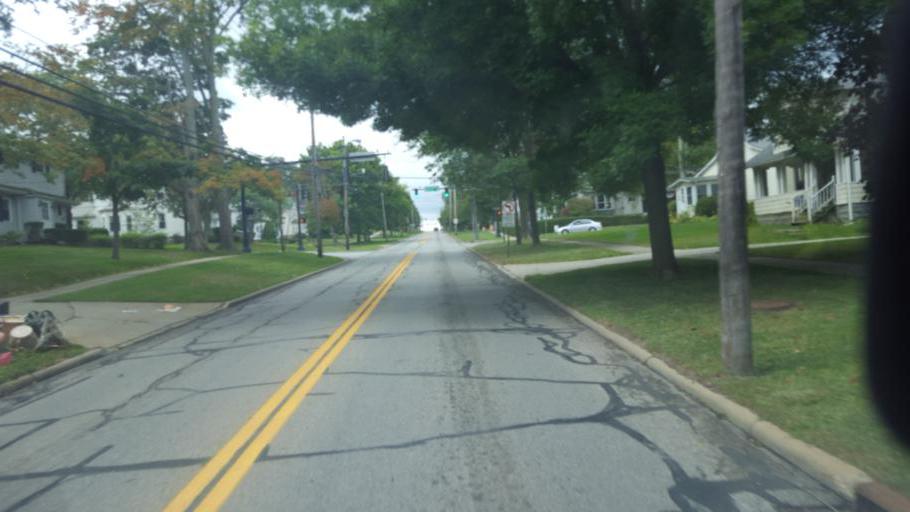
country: US
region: Ohio
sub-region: Geauga County
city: Chardon
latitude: 41.5835
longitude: -81.1981
